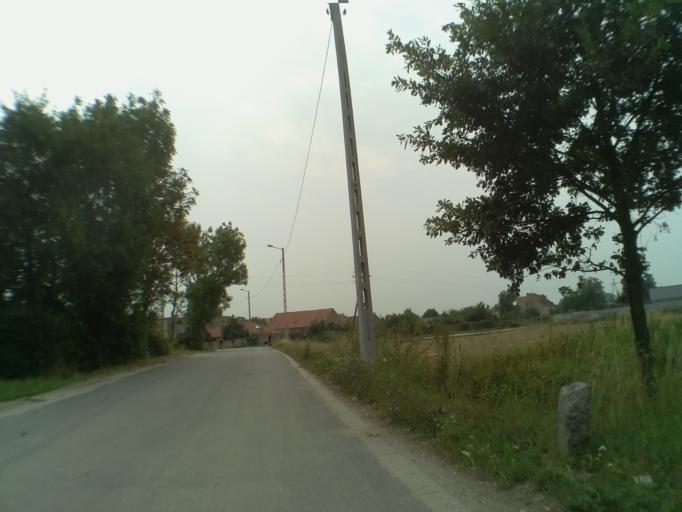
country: PL
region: Lower Silesian Voivodeship
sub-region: Powiat swidnicki
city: Strzegom
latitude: 50.9568
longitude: 16.3405
